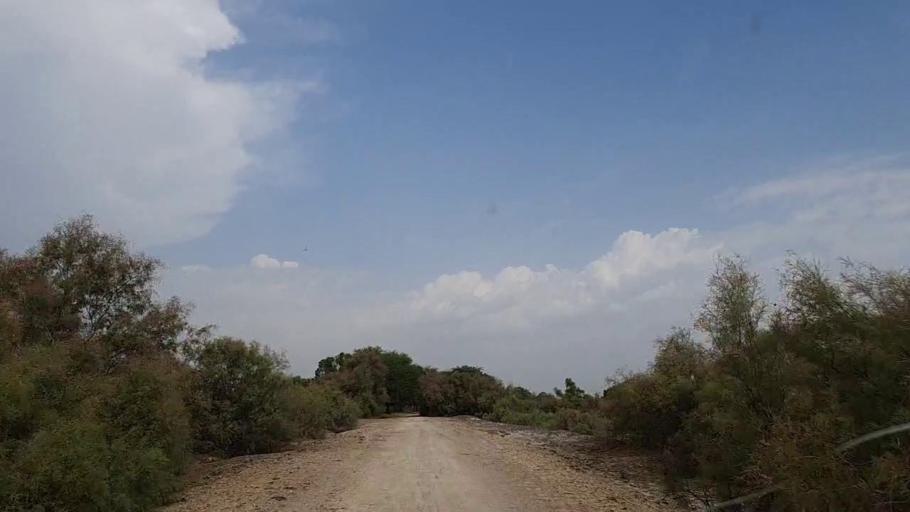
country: PK
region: Sindh
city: Khanpur
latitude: 27.8180
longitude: 69.5328
